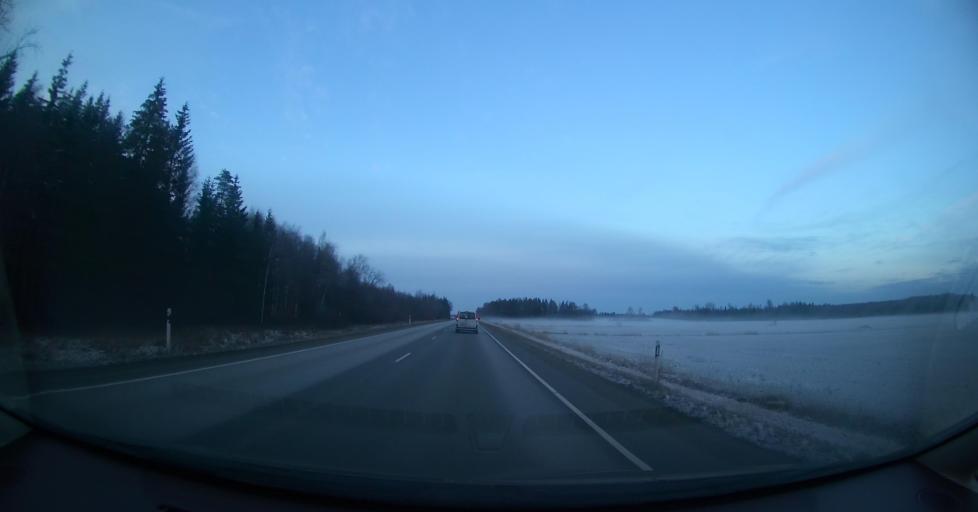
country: EE
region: Jogevamaa
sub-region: Poltsamaa linn
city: Poltsamaa
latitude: 58.7547
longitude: 25.7600
